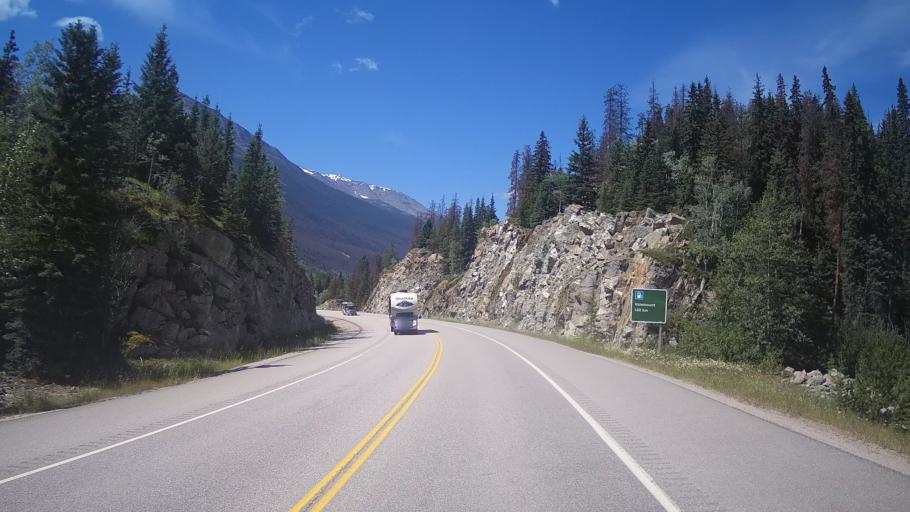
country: CA
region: Alberta
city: Jasper Park Lodge
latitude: 52.8651
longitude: -118.1014
